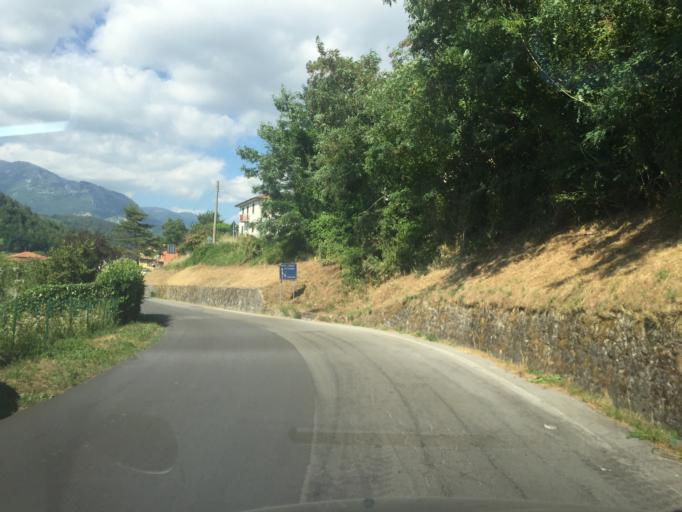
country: IT
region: Tuscany
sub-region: Provincia di Lucca
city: Camporgiano
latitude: 44.1448
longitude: 10.3522
